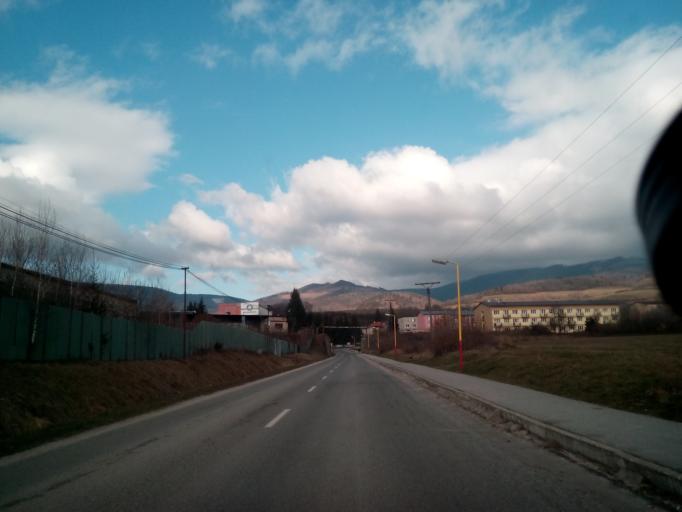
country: SK
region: Kosicky
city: Dobsina
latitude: 48.7161
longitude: 20.2748
